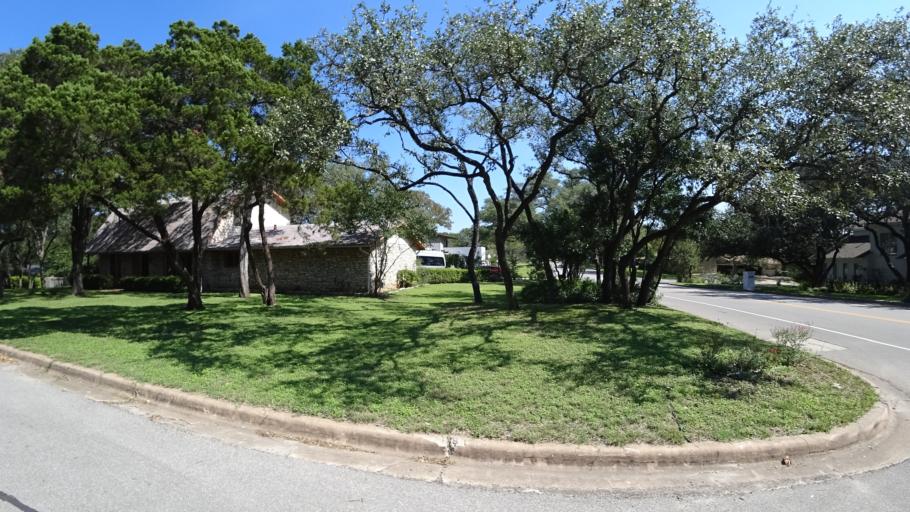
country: US
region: Texas
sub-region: Travis County
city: Rollingwood
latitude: 30.2743
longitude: -97.7898
